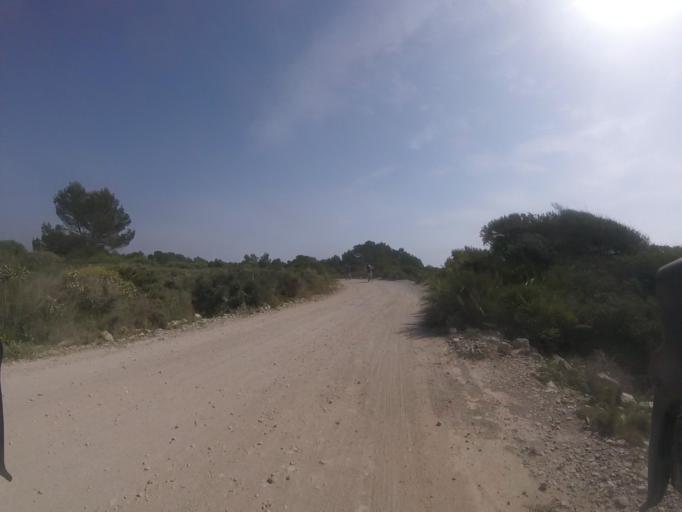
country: ES
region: Valencia
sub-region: Provincia de Castello
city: Santa Magdalena de Pulpis
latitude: 40.2959
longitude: 0.3445
